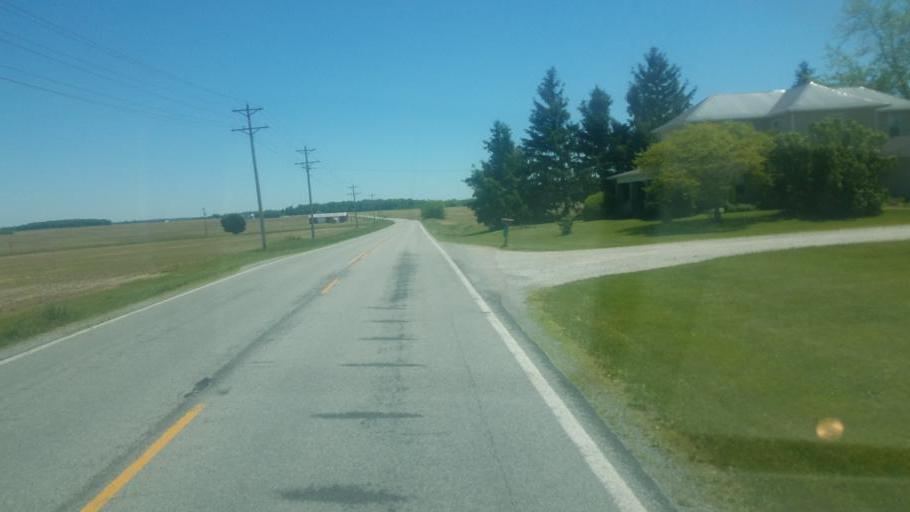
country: US
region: Ohio
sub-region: Miami County
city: Piqua
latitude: 40.2181
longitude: -84.3109
